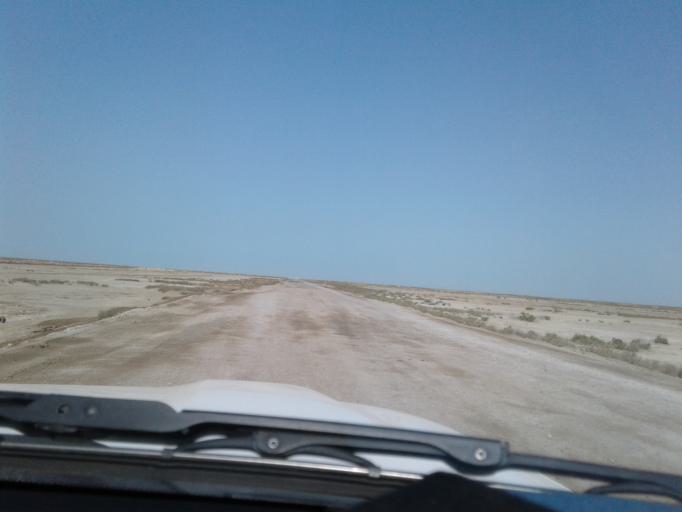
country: IR
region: Golestan
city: Gomishan
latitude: 37.8383
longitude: 53.8978
